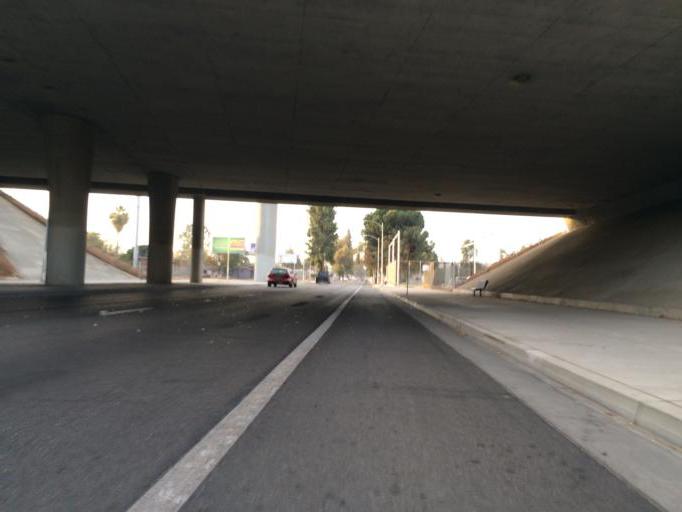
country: US
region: California
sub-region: Fresno County
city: Fresno
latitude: 36.7548
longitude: -119.7726
